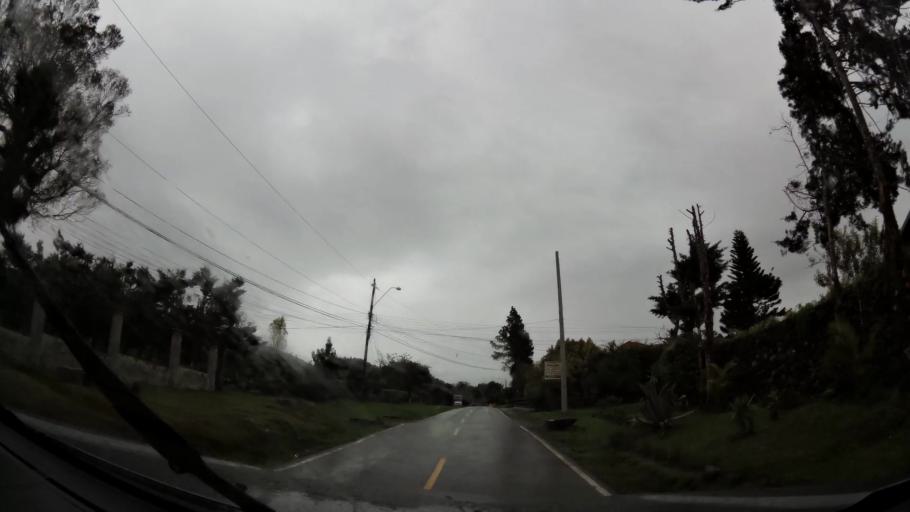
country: PA
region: Chiriqui
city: Volcan
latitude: 8.7896
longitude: -82.6525
